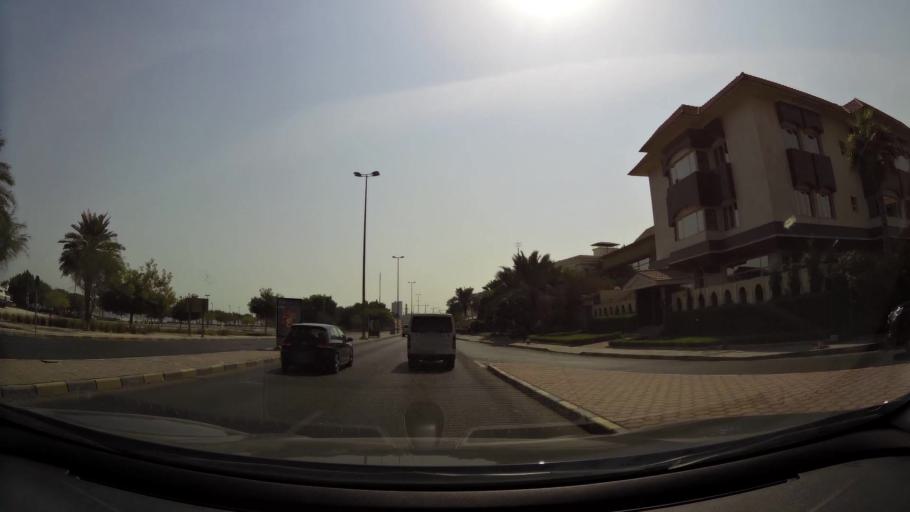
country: KW
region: Al Ahmadi
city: Al Manqaf
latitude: 29.0917
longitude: 48.1376
